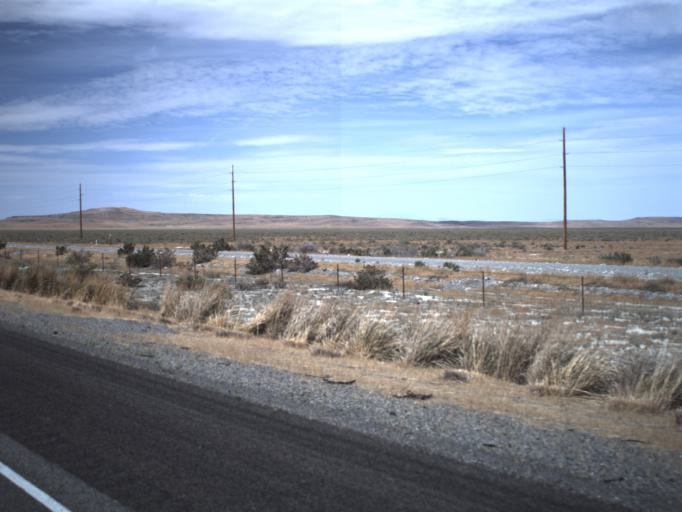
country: US
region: Utah
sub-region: Tooele County
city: Grantsville
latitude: 40.7452
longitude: -113.0675
